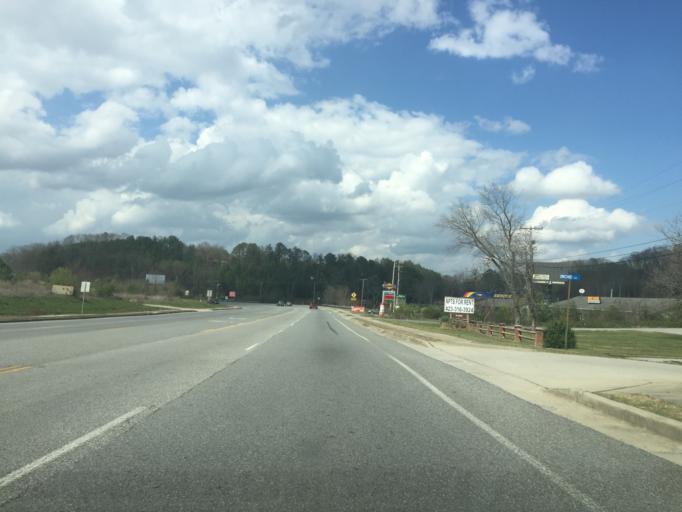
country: US
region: Georgia
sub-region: Catoosa County
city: Indian Springs
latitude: 34.9829
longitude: -85.1873
